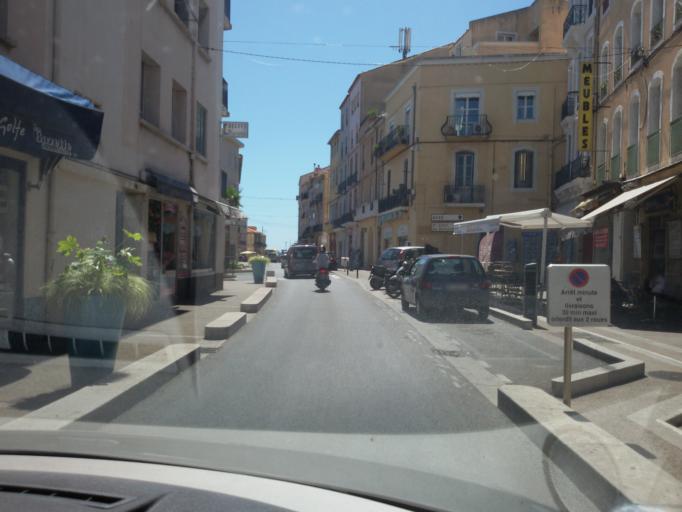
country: FR
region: Languedoc-Roussillon
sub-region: Departement de l'Herault
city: Sete
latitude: 43.3996
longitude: 3.6961
